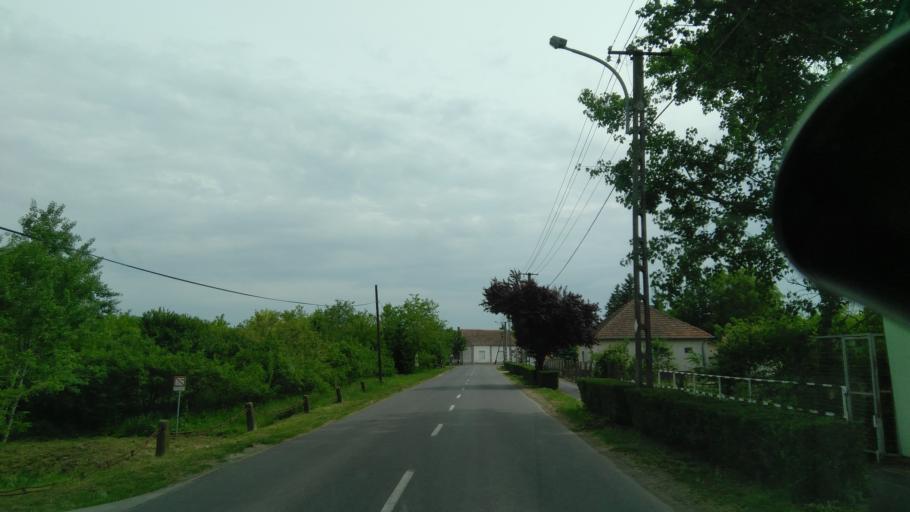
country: HU
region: Bekes
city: Sarkad
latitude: 46.8121
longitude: 21.3832
